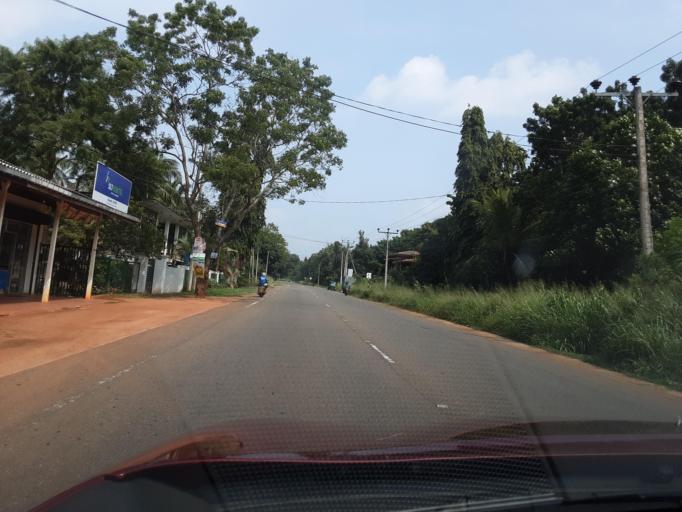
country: LK
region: North Central
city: Anuradhapura
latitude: 8.3415
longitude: 80.5043
